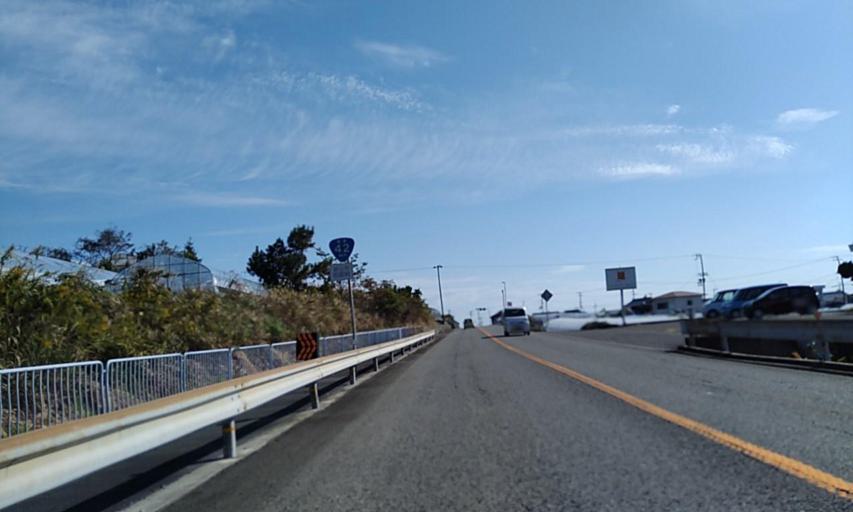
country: JP
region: Wakayama
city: Gobo
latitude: 33.8243
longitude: 135.1902
